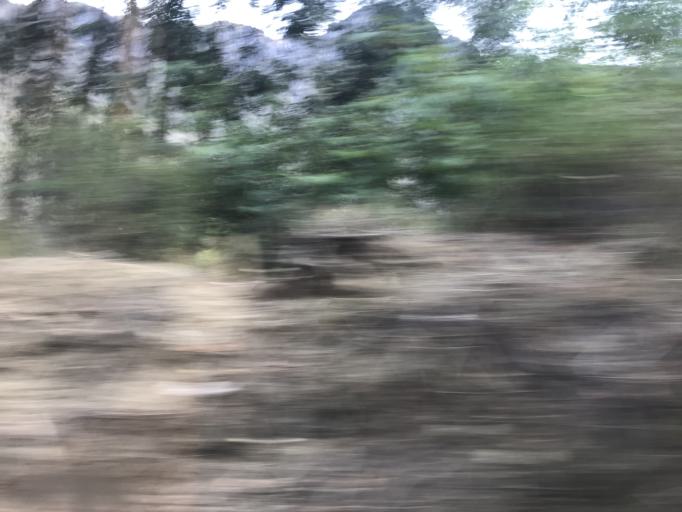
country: PE
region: Cusco
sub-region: Provincia de Urubamba
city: Ollantaytambo
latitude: -13.2529
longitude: -72.2823
